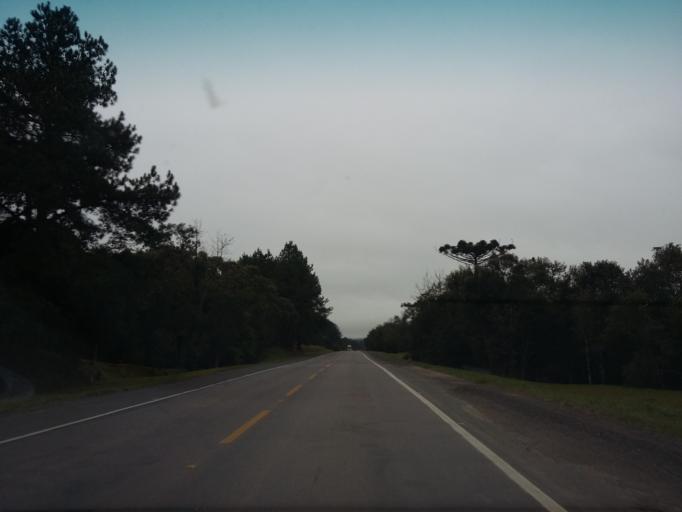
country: BR
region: Santa Catarina
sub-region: Santa Cecilia
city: Santa Cecilia
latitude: -26.6302
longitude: -50.2462
